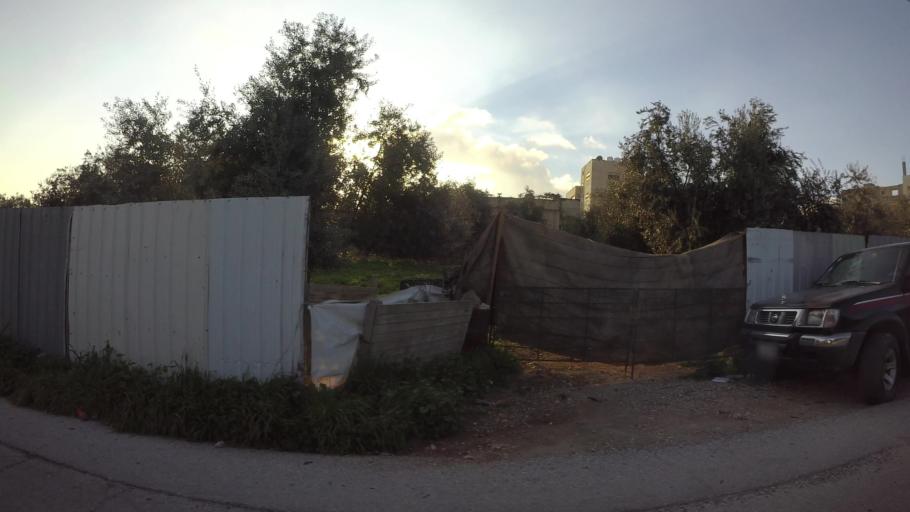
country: JO
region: Amman
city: Al Bunayyat ash Shamaliyah
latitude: 31.9040
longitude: 35.9079
